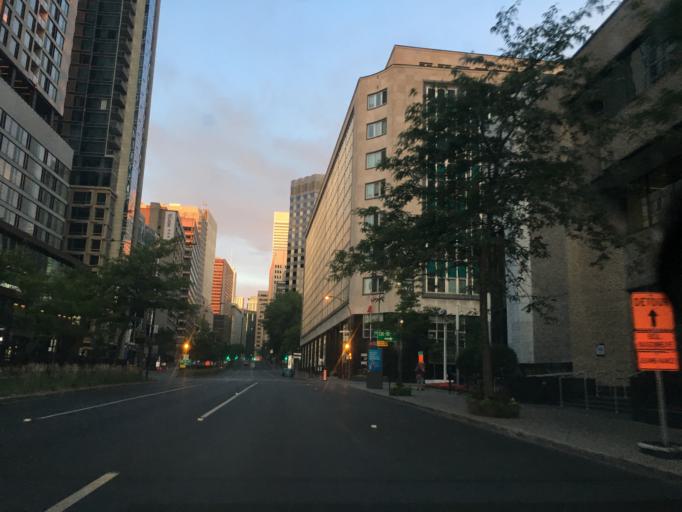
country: CA
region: Quebec
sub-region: Montreal
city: Montreal
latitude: 45.5068
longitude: -73.5636
